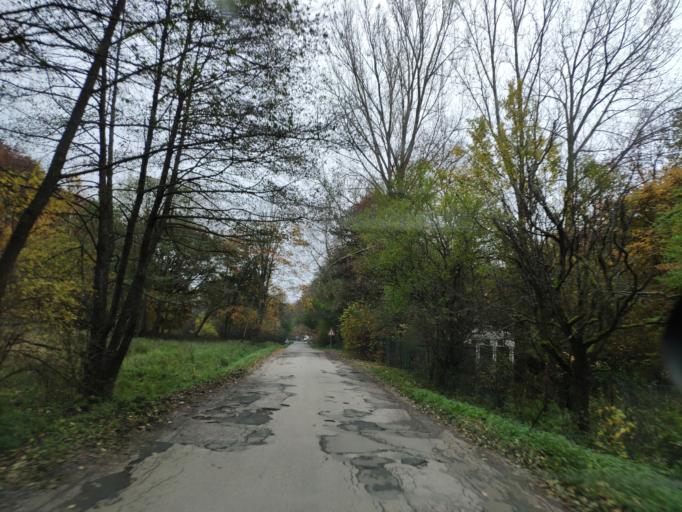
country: SK
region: Kosicky
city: Moldava nad Bodvou
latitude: 48.7324
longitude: 21.0308
